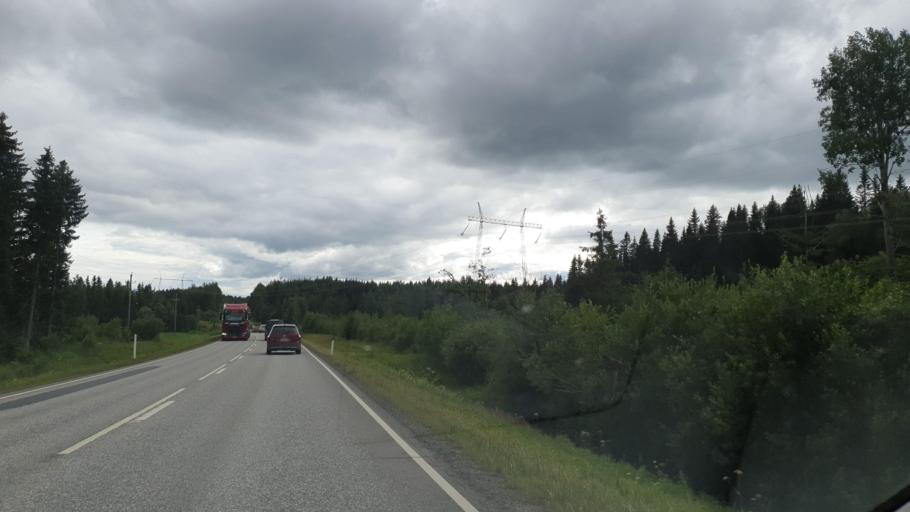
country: FI
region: Northern Savo
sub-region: Ylae-Savo
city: Sonkajaervi
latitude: 63.7096
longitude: 27.3588
